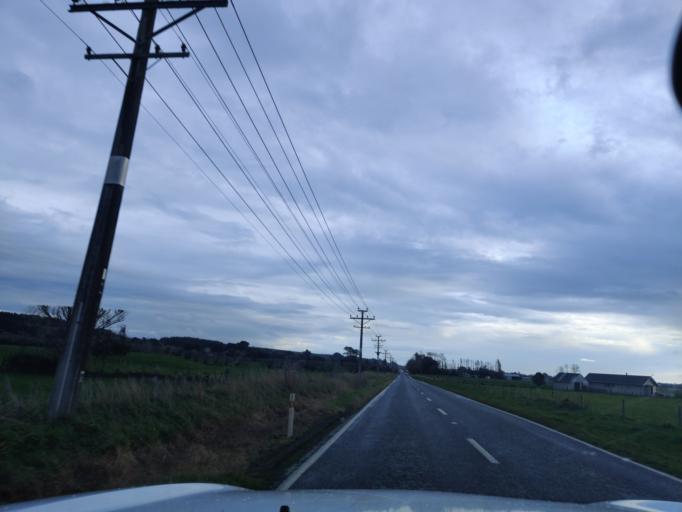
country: NZ
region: Manawatu-Wanganui
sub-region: Palmerston North City
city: Palmerston North
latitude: -40.3455
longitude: 175.7083
